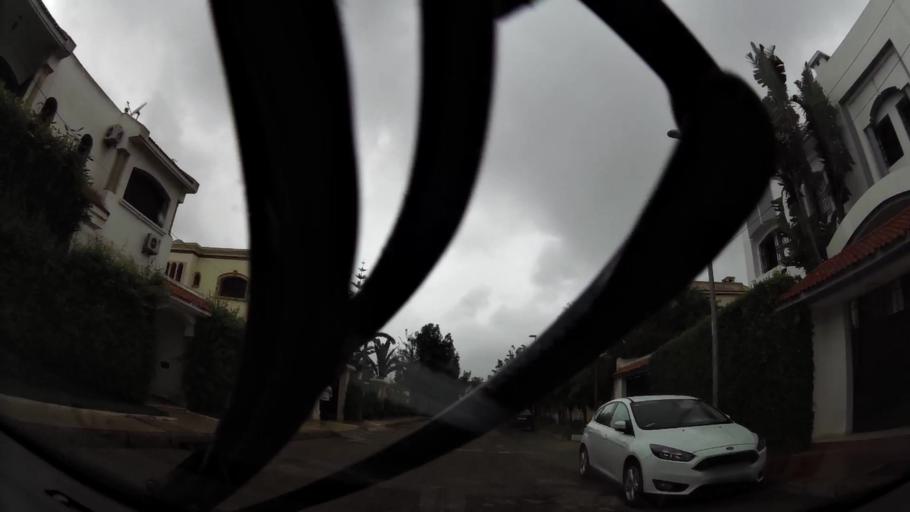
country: MA
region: Grand Casablanca
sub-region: Casablanca
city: Casablanca
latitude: 33.5325
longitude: -7.6202
